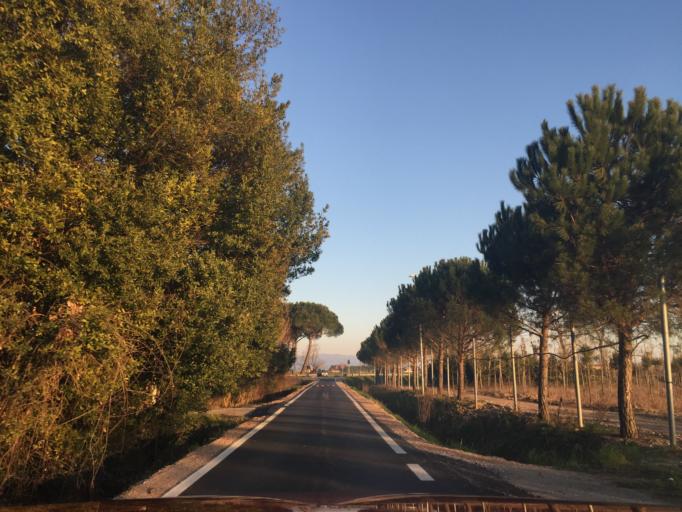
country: IT
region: Tuscany
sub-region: Provincia di Pistoia
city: Ponte Buggianese
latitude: 43.8580
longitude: 10.7660
